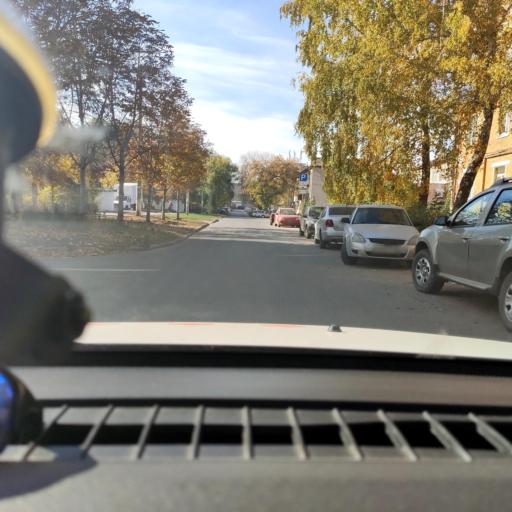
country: RU
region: Samara
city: Samara
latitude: 53.2170
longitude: 50.2336
